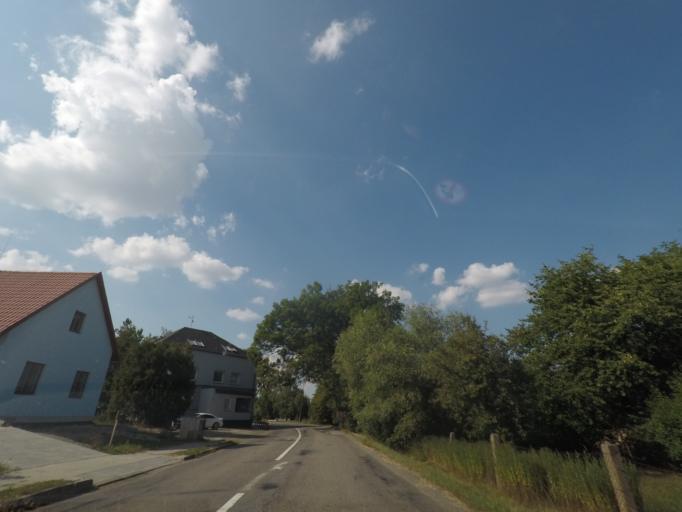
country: CZ
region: Kralovehradecky
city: Dolni Cernilov
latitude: 50.2406
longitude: 15.9670
